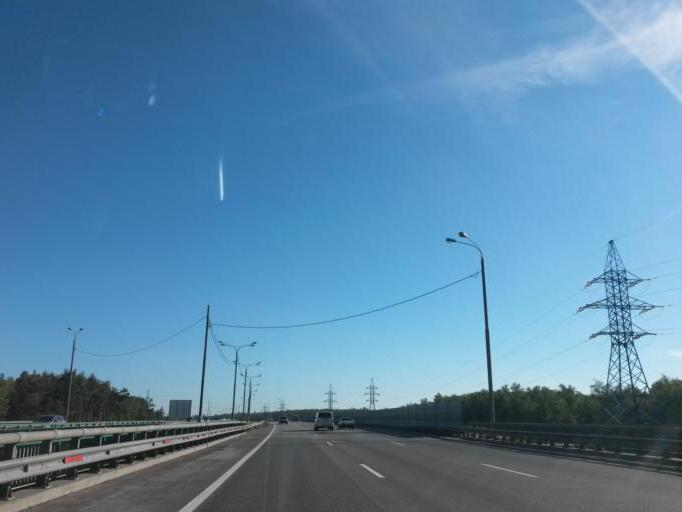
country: RU
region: Moskovskaya
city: Vostryakovo
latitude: 55.4125
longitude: 37.7926
